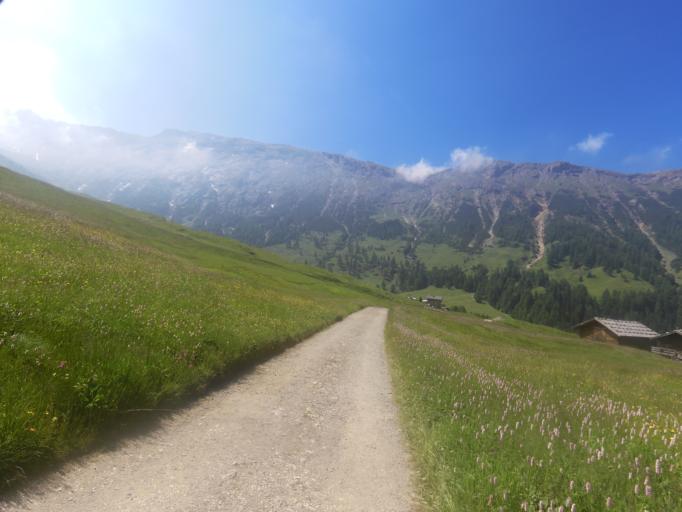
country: IT
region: Trentino-Alto Adige
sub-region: Bolzano
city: Siusi
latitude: 46.5165
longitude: 11.6087
